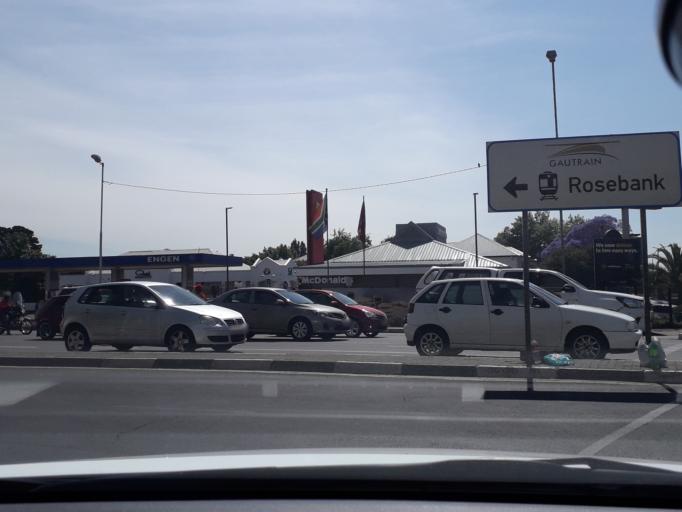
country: ZA
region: Gauteng
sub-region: City of Johannesburg Metropolitan Municipality
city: Johannesburg
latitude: -26.1491
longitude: 28.0446
